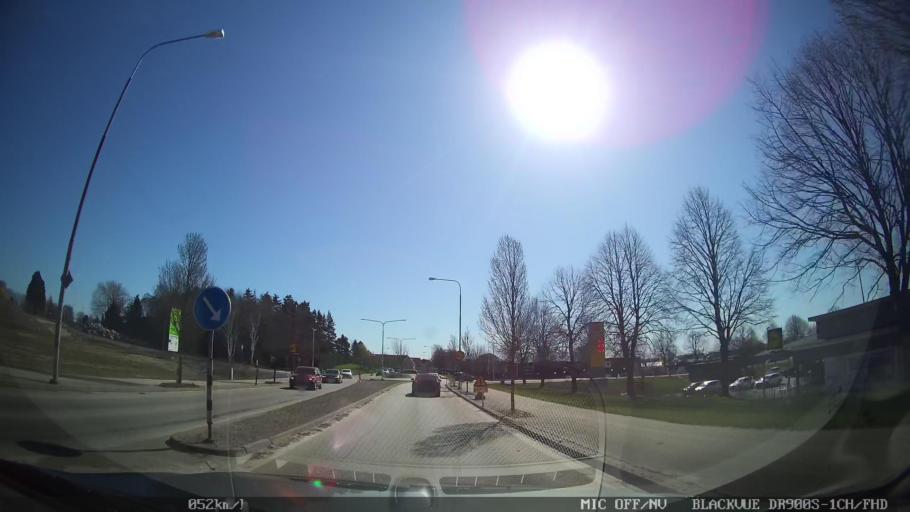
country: SE
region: Skane
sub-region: Ystads Kommun
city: Ystad
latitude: 55.4337
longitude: 13.8002
